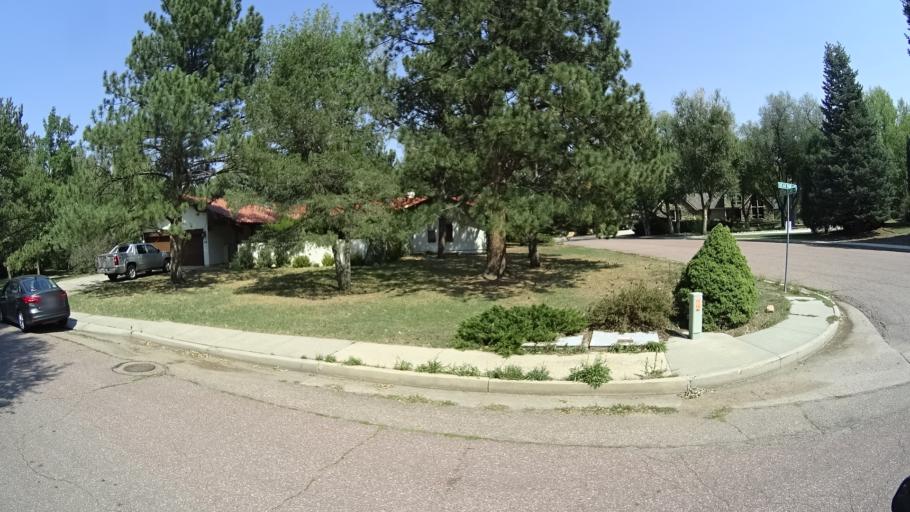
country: US
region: Colorado
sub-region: El Paso County
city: Colorado Springs
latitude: 38.8010
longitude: -104.8369
